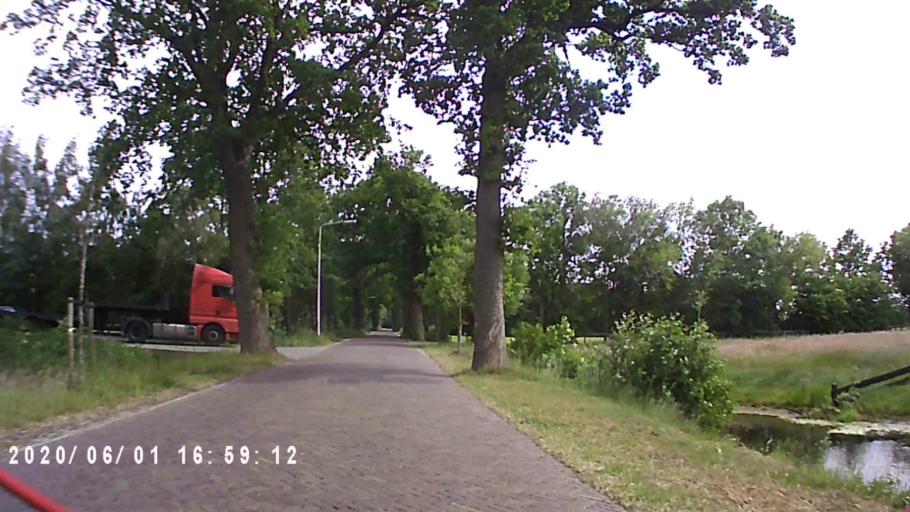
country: NL
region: Friesland
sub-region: Gemeente Tytsjerksteradiel
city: Hurdegaryp
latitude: 53.1869
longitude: 5.9277
